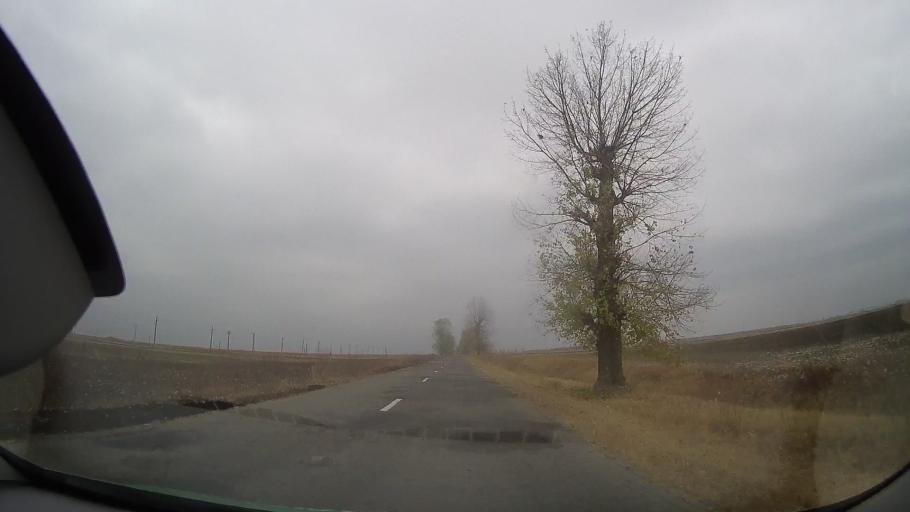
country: RO
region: Ialomita
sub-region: Comuna Grindu
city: Grindu
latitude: 44.7992
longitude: 26.8818
